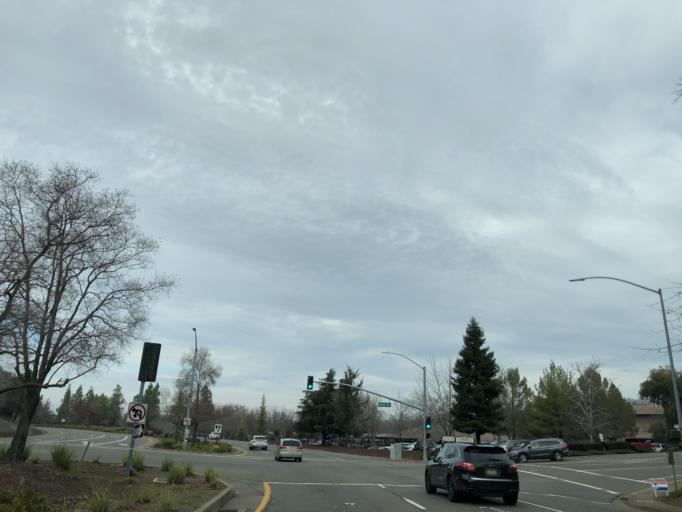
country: US
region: California
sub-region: El Dorado County
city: El Dorado Hills
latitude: 38.6816
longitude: -121.0759
